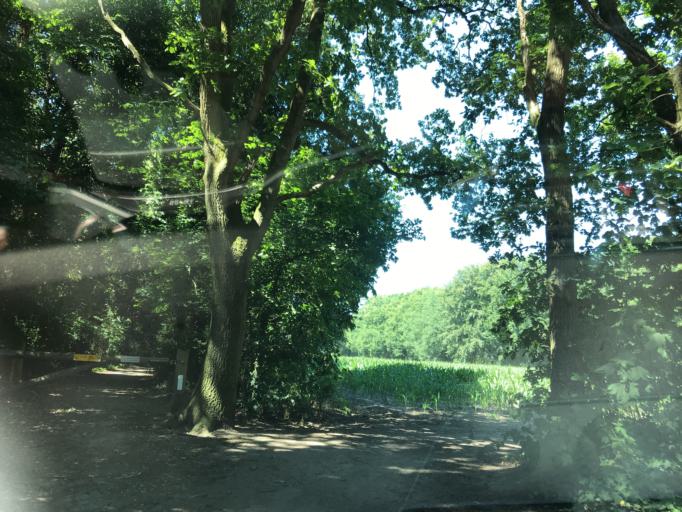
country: NL
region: North Holland
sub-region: Gemeente Huizen
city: Huizen
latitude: 52.3016
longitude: 5.2196
